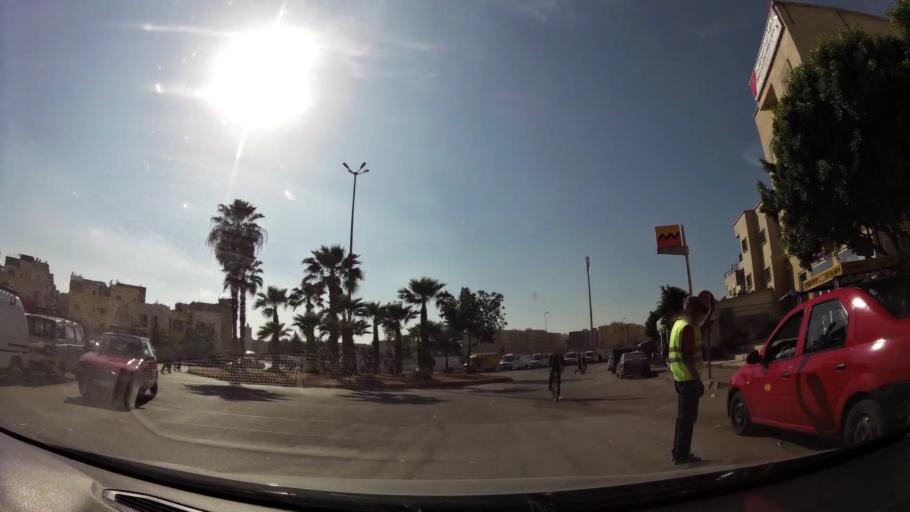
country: MA
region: Fes-Boulemane
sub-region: Fes
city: Fes
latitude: 34.0191
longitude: -5.0342
